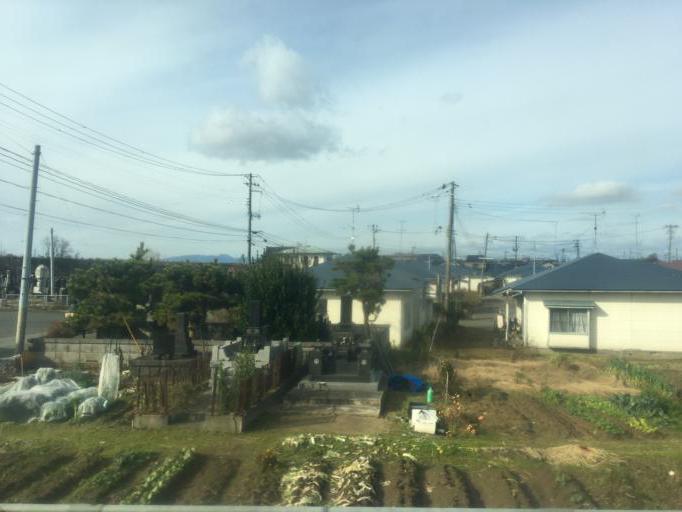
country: JP
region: Akita
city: Tenno
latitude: 39.8630
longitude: 140.0598
